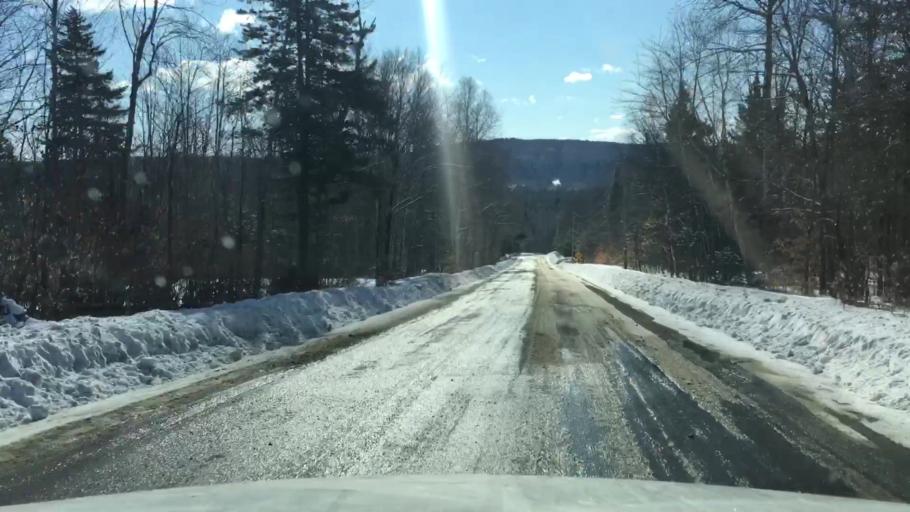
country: US
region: Maine
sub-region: Washington County
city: Calais
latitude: 45.0745
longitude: -67.5013
